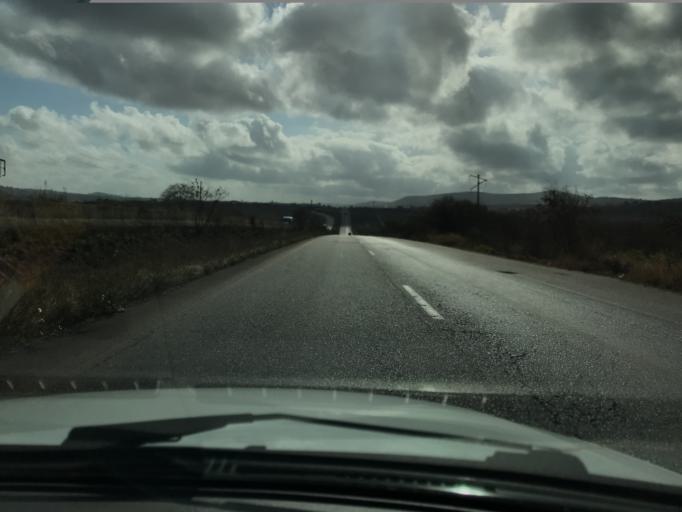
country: BR
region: Pernambuco
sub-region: Gravata
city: Gravata
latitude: -8.2152
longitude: -35.6369
